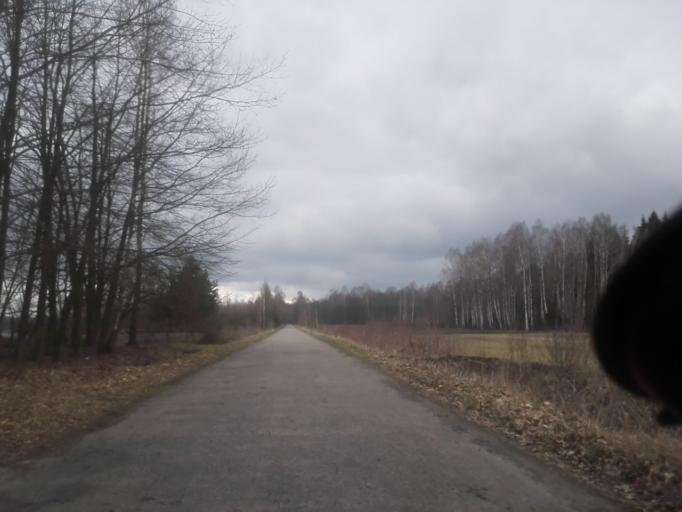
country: PL
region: Podlasie
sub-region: Powiat sejnenski
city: Punsk
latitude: 54.2548
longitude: 23.0159
